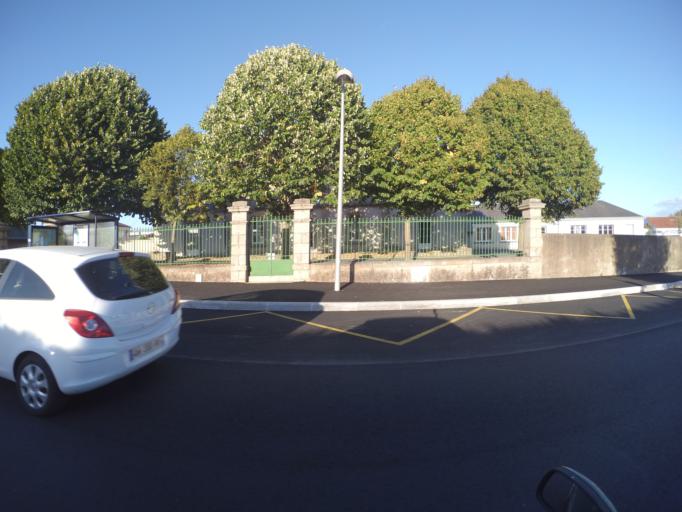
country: FR
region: Pays de la Loire
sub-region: Departement de la Vendee
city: Saint-Hilaire-de-Loulay
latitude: 47.0037
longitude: -1.3333
